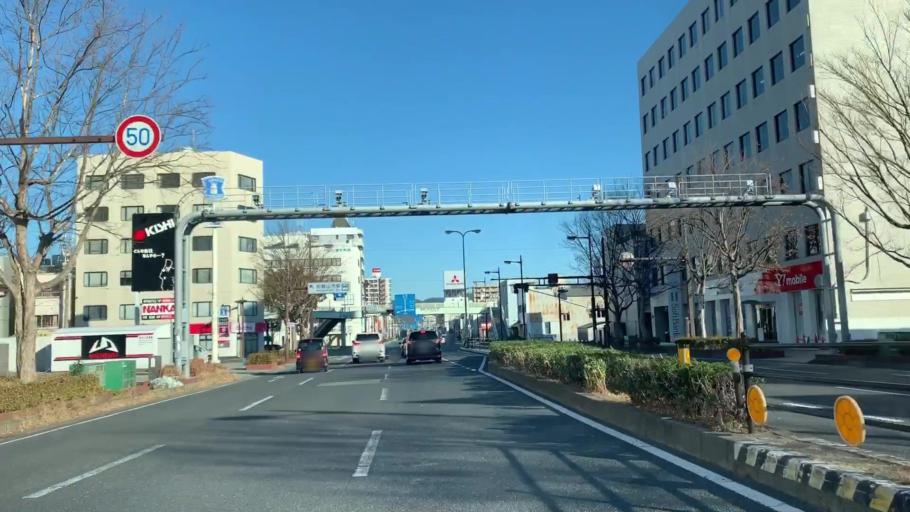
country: JP
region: Wakayama
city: Wakayama-shi
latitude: 34.2330
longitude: 135.1695
